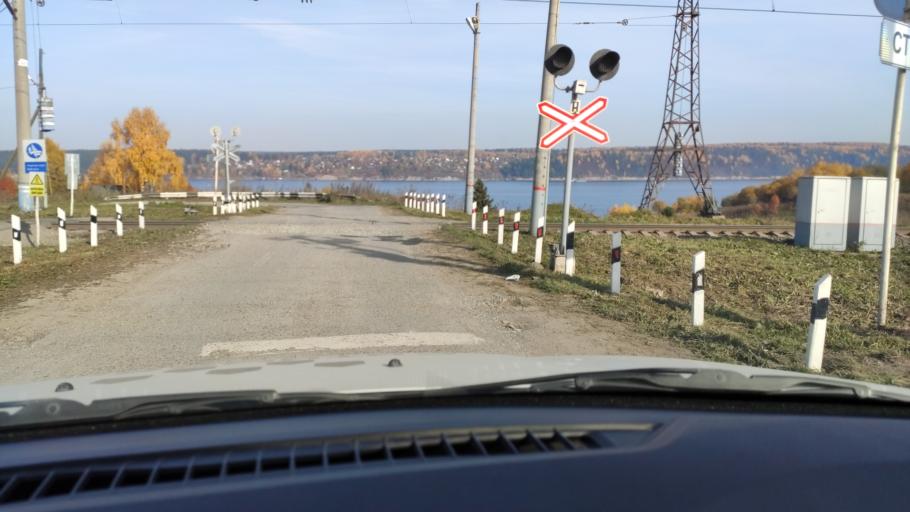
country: RU
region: Perm
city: Sylva
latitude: 58.0417
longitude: 56.7493
